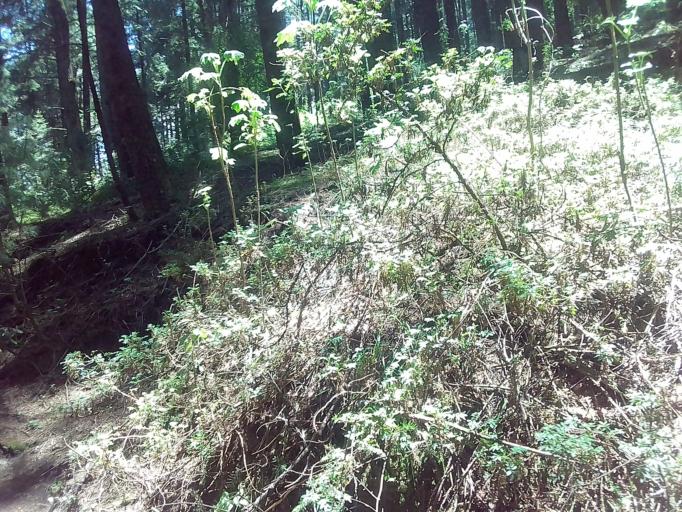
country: MX
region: Mexico City
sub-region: Cuajimalpa de Morelos
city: San Lorenzo Acopilco
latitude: 19.2896
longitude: -99.3349
